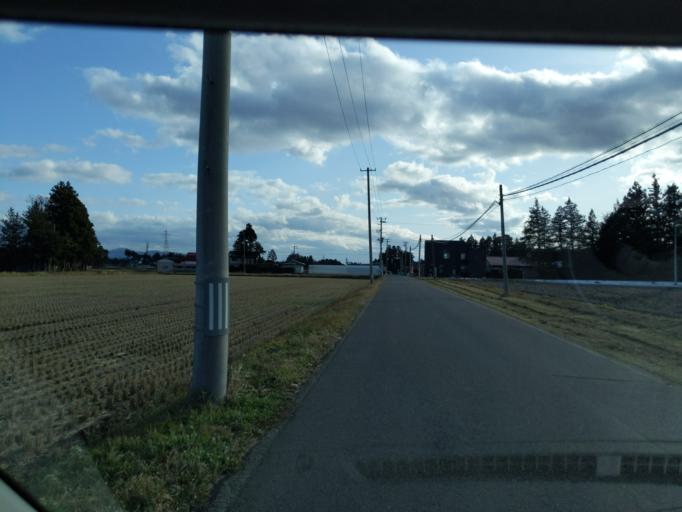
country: JP
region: Iwate
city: Mizusawa
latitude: 39.1385
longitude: 141.0798
